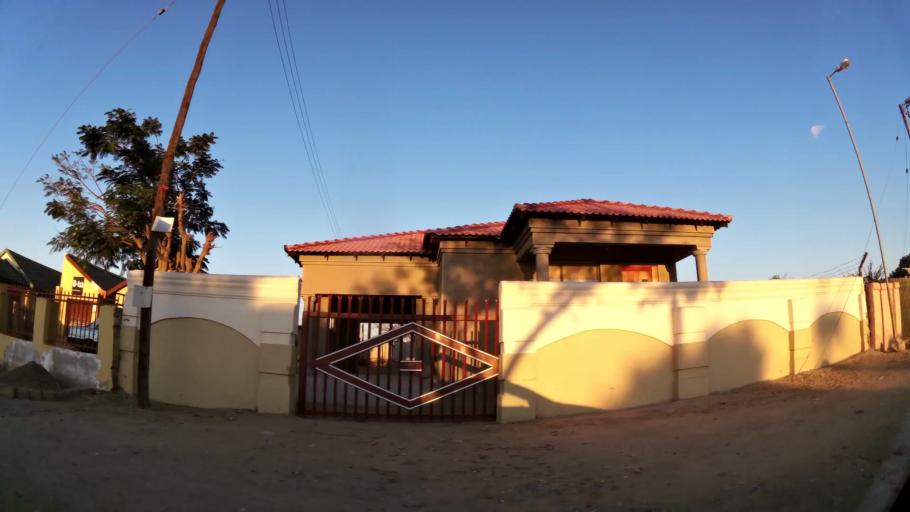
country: ZA
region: Limpopo
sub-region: Capricorn District Municipality
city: Polokwane
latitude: -23.8591
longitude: 29.3721
